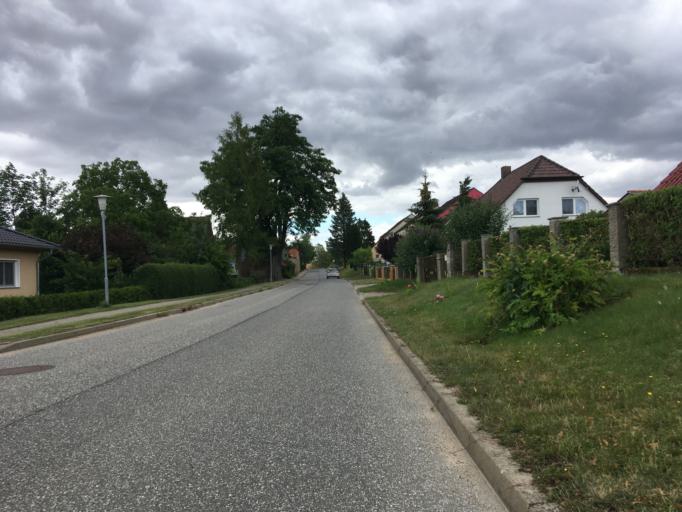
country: DE
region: Brandenburg
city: Grunow
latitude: 53.2458
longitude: 13.9439
